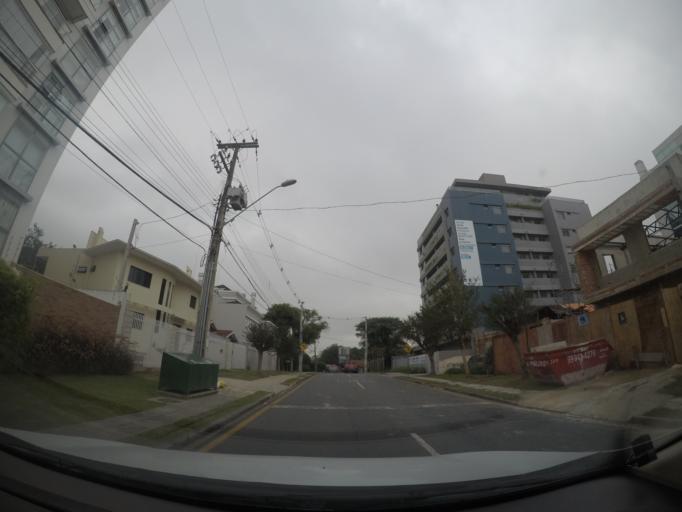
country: BR
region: Parana
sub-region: Curitiba
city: Curitiba
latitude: -25.4033
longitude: -49.2600
